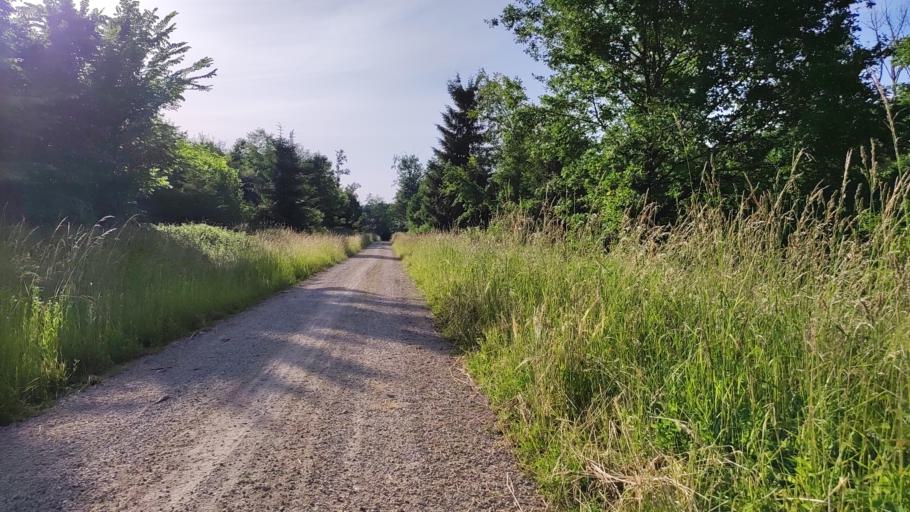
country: DE
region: Bavaria
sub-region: Swabia
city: Landensberg
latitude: 48.4273
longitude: 10.5113
